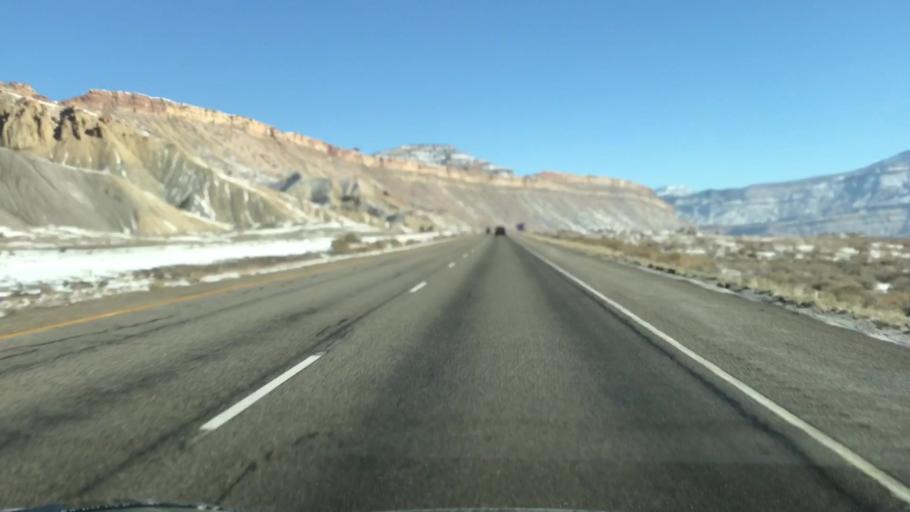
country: US
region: Colorado
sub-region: Mesa County
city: Clifton
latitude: 39.1139
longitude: -108.4041
